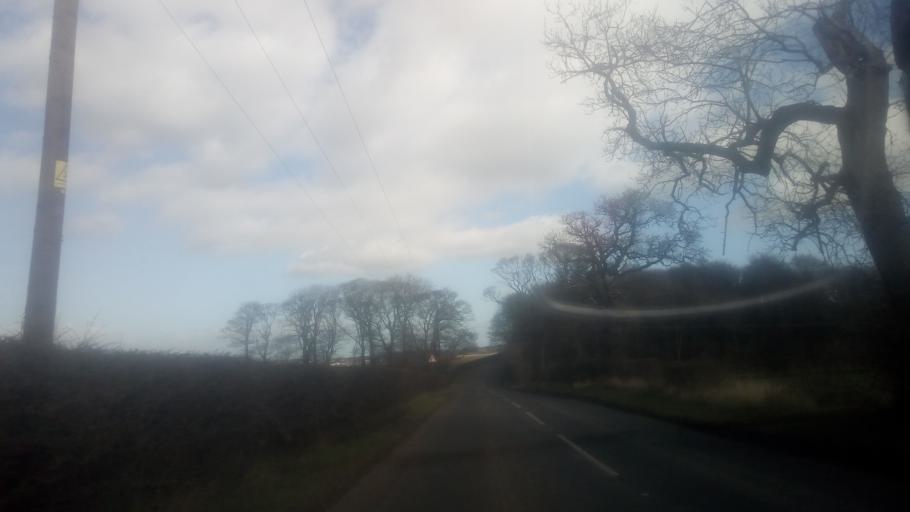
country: GB
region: Scotland
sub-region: East Lothian
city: Ormiston
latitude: 55.9007
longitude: -2.9475
